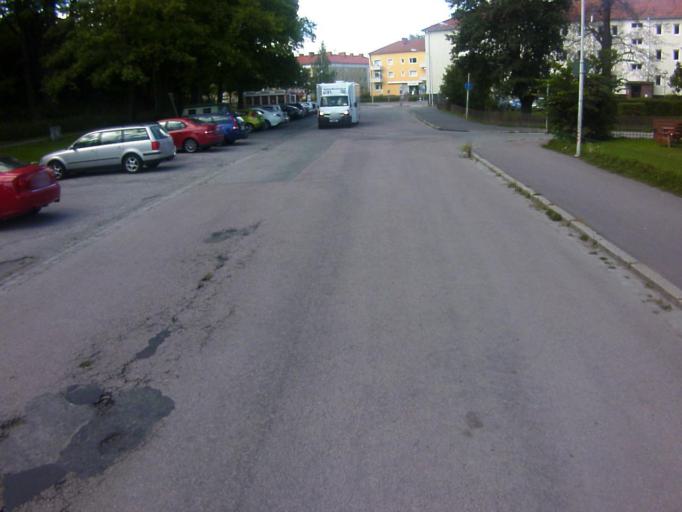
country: SE
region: Soedermanland
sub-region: Eskilstuna Kommun
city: Eskilstuna
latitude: 59.3697
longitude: 16.5351
